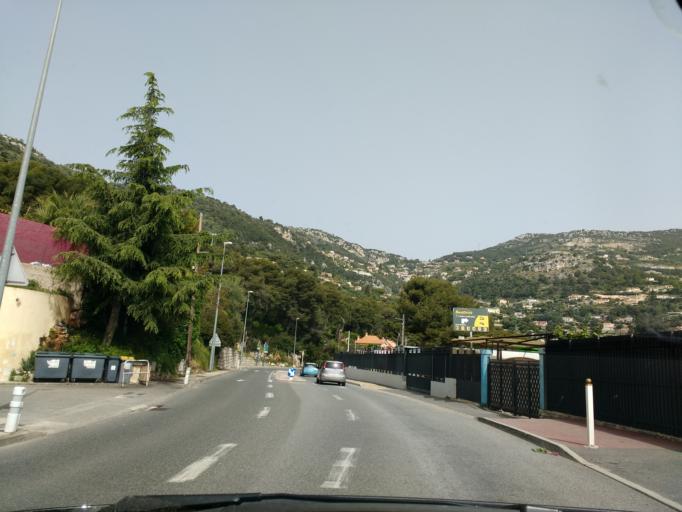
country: MC
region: Commune de Monaco
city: Moneghetti
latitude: 43.7361
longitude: 7.4131
